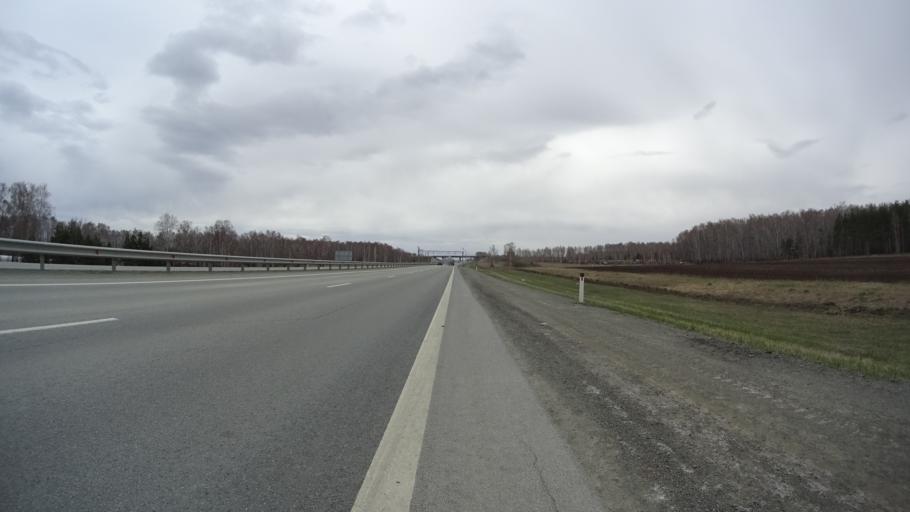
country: RU
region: Chelyabinsk
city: Yemanzhelinka
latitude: 54.8202
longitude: 61.3089
